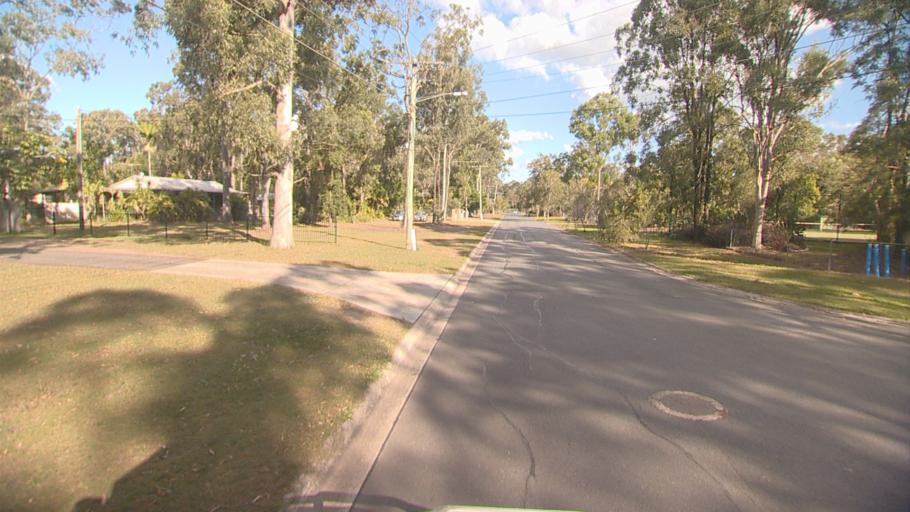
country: AU
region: Queensland
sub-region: Logan
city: Beenleigh
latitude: -27.6683
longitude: 153.2078
